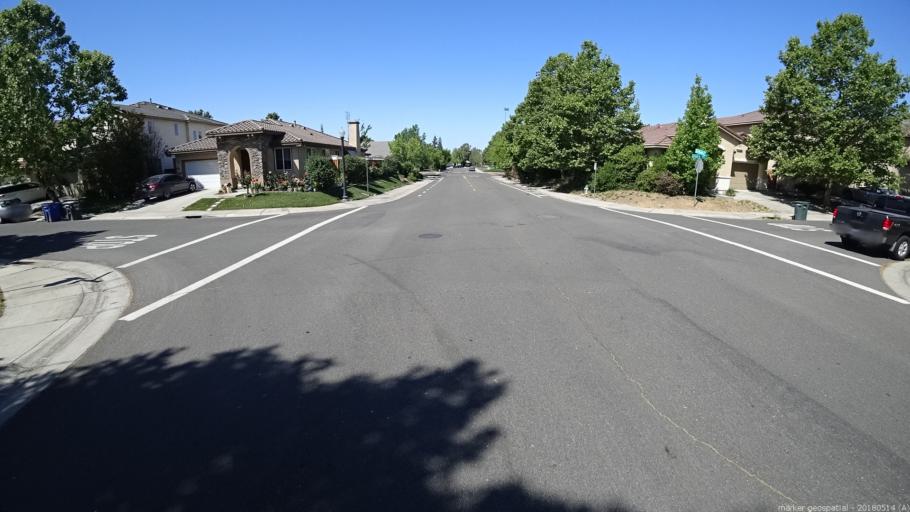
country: US
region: California
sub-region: Yolo County
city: West Sacramento
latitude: 38.6374
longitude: -121.5284
